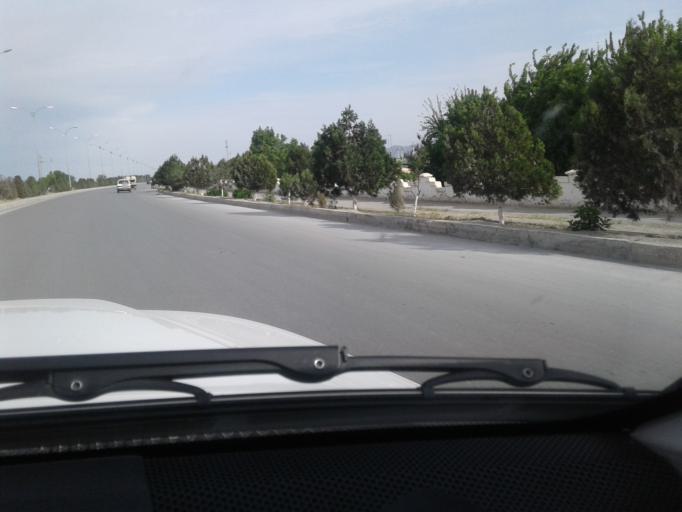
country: TM
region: Ahal
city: Abadan
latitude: 38.1555
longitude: 57.9735
